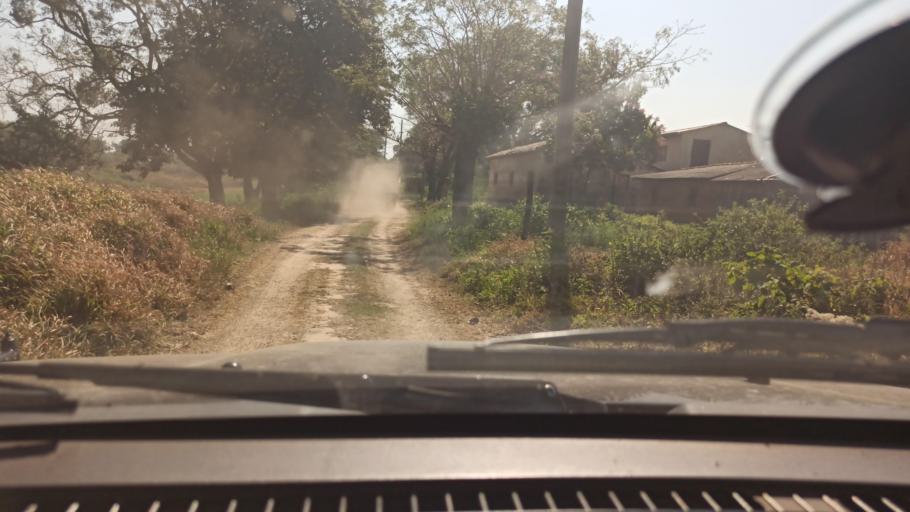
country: PY
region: Asuncion
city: Asuncion
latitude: -25.3367
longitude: -57.6805
